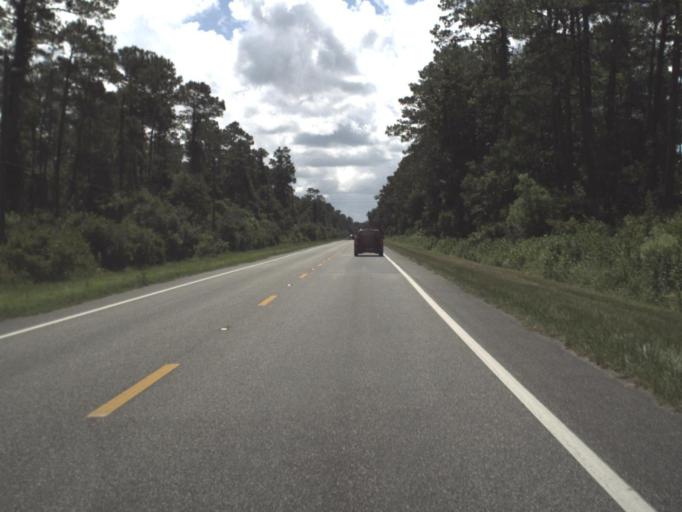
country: US
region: Florida
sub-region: Putnam County
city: Crescent City
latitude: 29.4820
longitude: -81.5554
